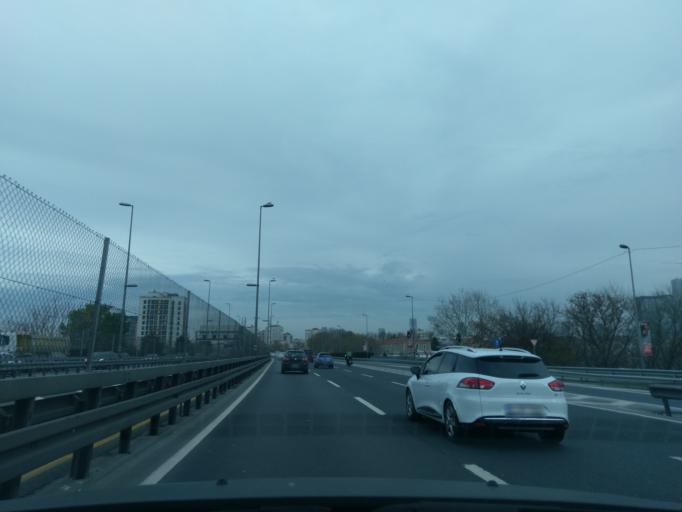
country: TR
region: Istanbul
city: Sisli
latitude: 41.0571
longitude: 28.9623
